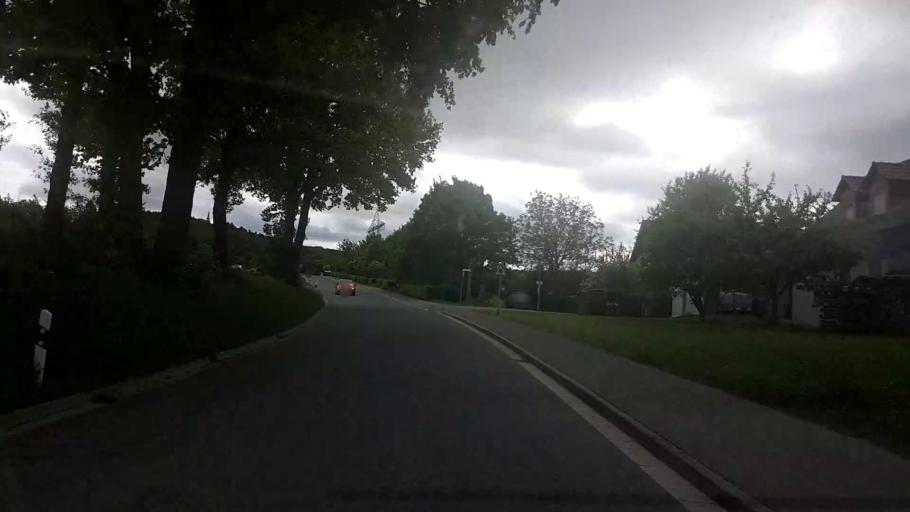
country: DE
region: Bavaria
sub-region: Upper Franconia
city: Lichtenfels
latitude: 50.1210
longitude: 11.0396
